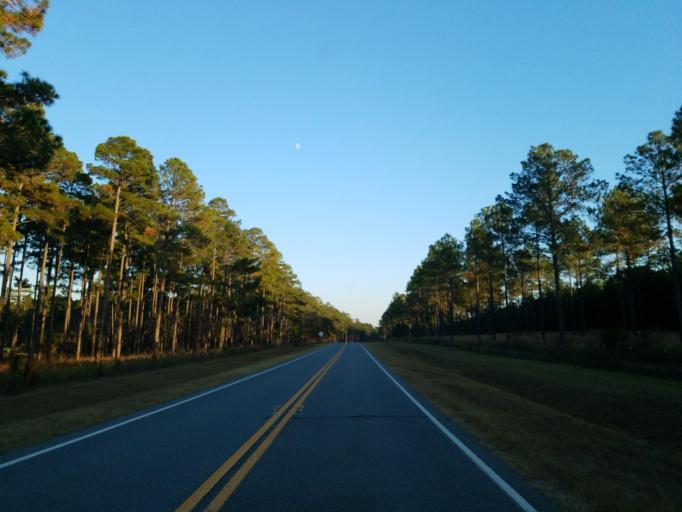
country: US
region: Georgia
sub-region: Wilcox County
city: Rochelle
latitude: 31.8233
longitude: -83.5474
